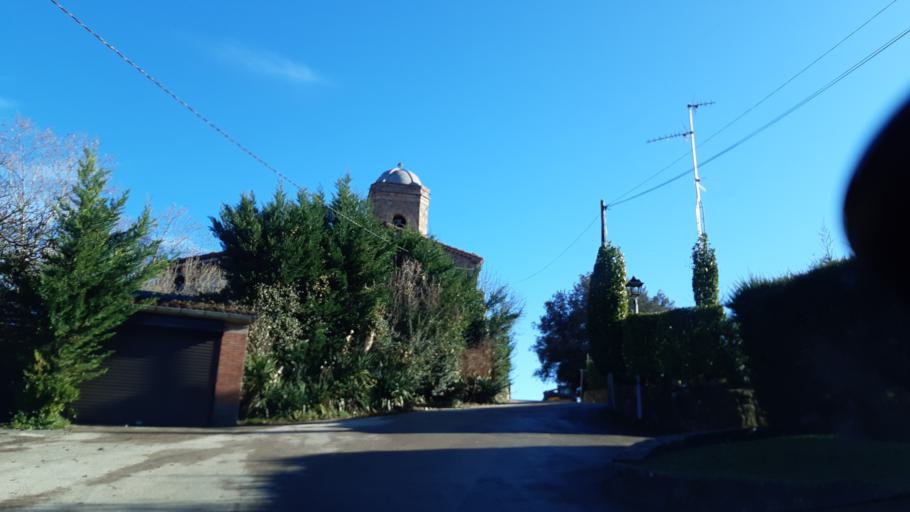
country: ES
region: Catalonia
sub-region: Provincia de Girona
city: Bas
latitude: 42.1499
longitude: 2.4387
